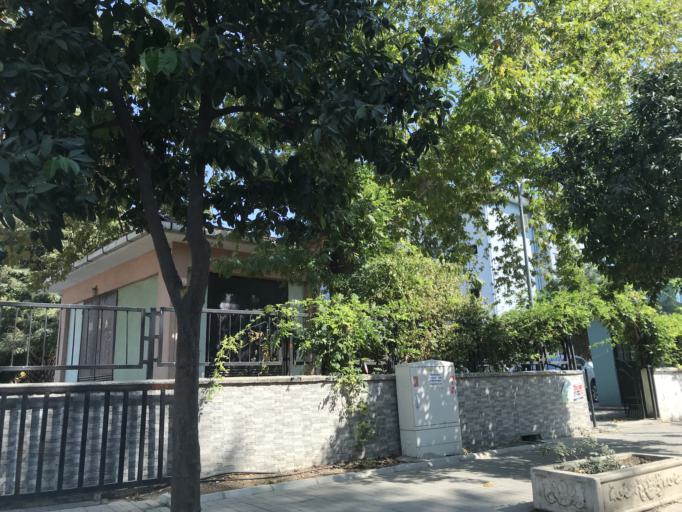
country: TR
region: Izmir
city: Selcuk
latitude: 37.9469
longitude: 27.3698
